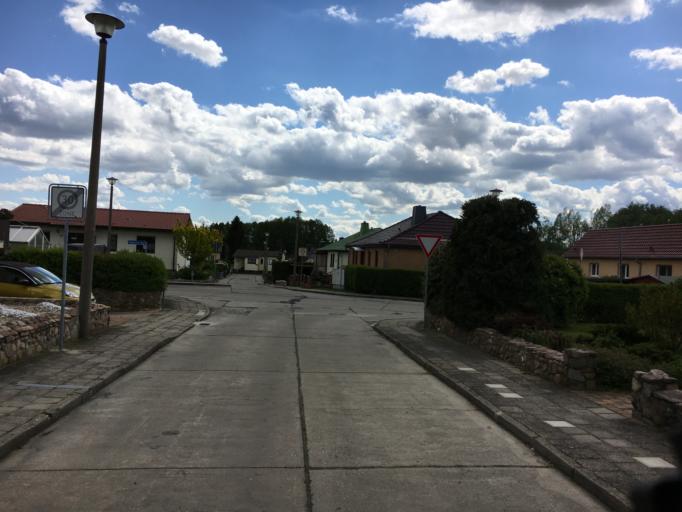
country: DE
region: Brandenburg
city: Juterbog
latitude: 52.0002
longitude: 13.0918
